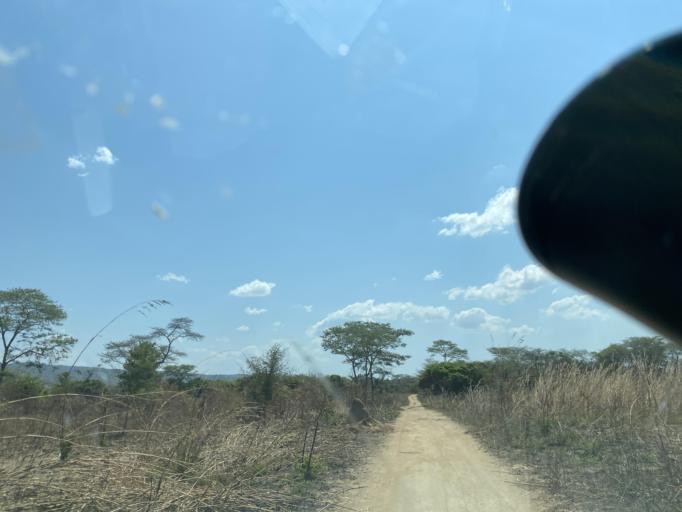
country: ZM
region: Lusaka
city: Chongwe
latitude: -15.0816
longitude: 29.5076
